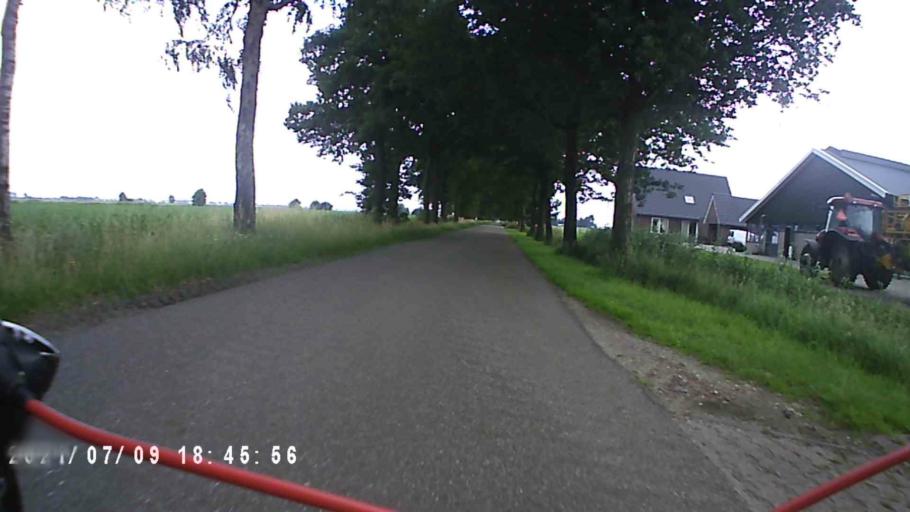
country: NL
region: Groningen
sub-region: Gemeente Veendam
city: Veendam
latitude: 53.0759
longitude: 6.9163
